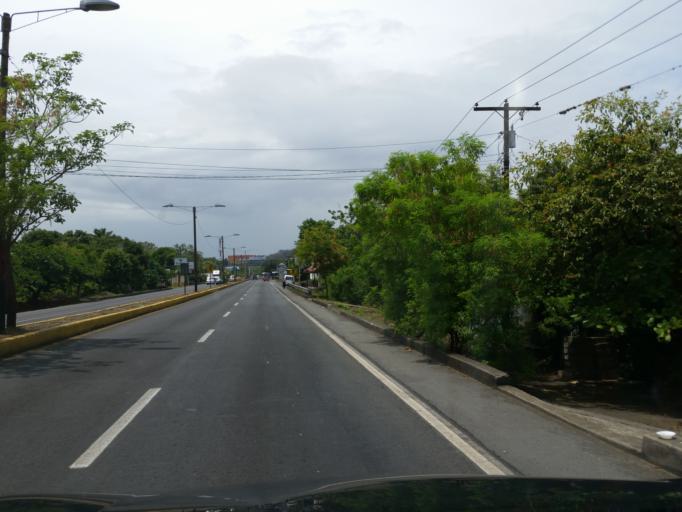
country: NI
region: Masaya
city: Nindiri
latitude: 11.9996
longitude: -86.1195
